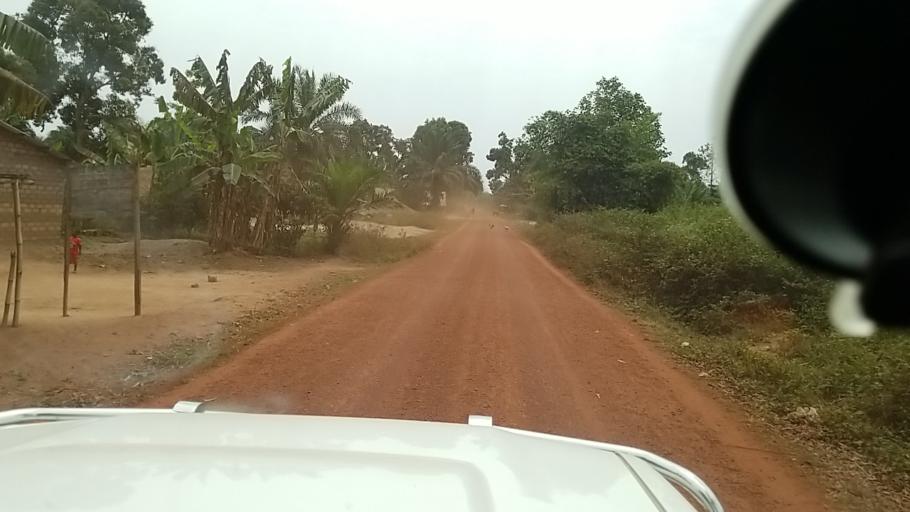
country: CD
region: Equateur
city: Libenge
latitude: 3.7237
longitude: 18.7707
